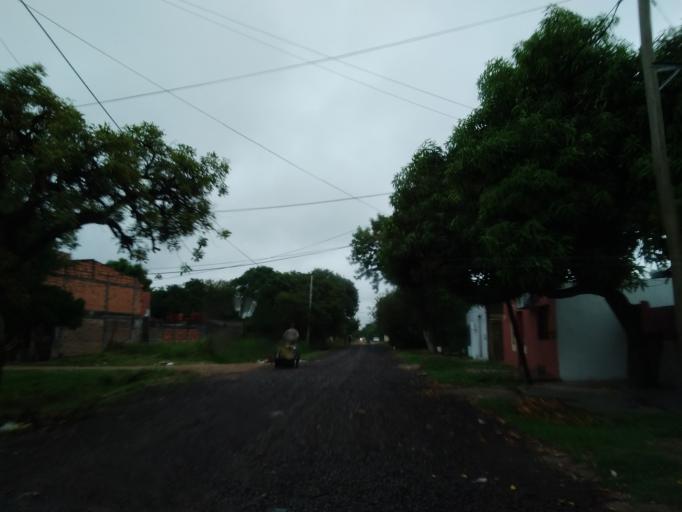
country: AR
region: Corrientes
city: Corrientes
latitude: -27.4897
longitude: -58.8192
